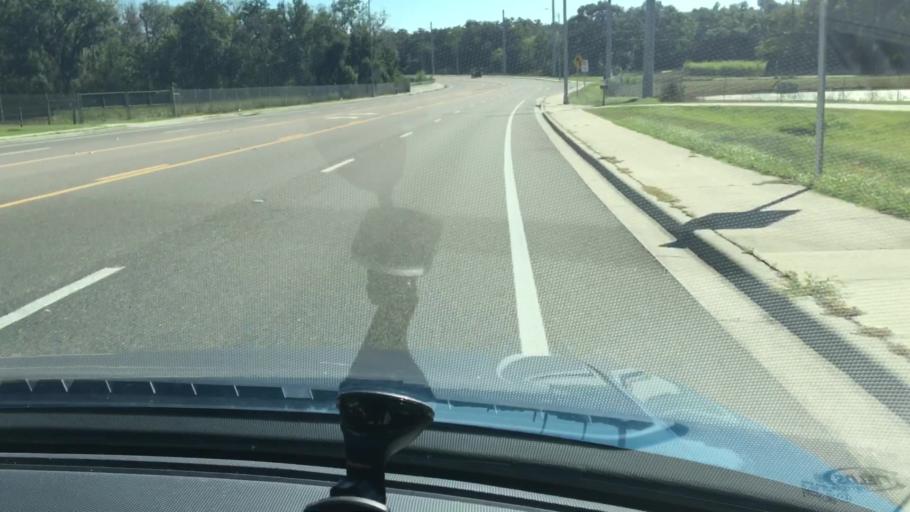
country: US
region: Florida
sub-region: Polk County
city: Kathleen
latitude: 28.1202
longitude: -82.0232
